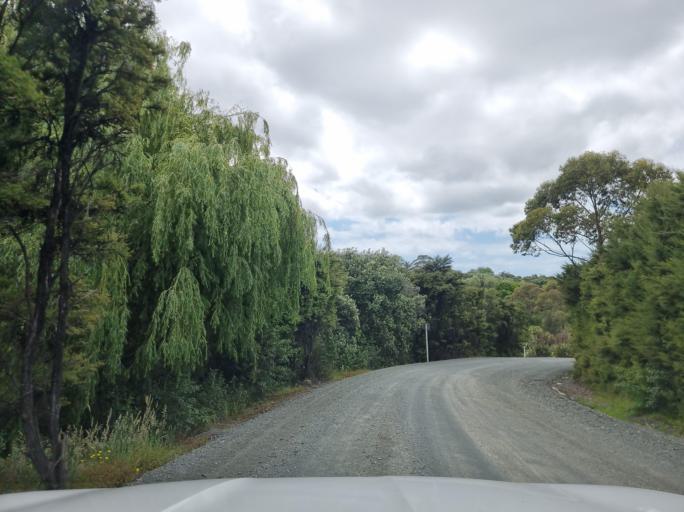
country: NZ
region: Auckland
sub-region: Auckland
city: Wellsford
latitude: -36.0900
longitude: 174.5289
